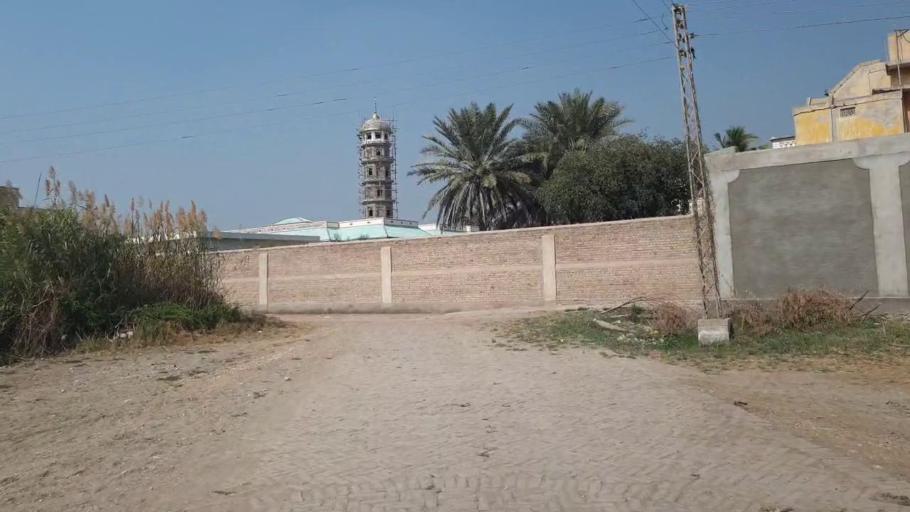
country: PK
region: Sindh
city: Chambar
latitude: 25.3738
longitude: 68.8797
